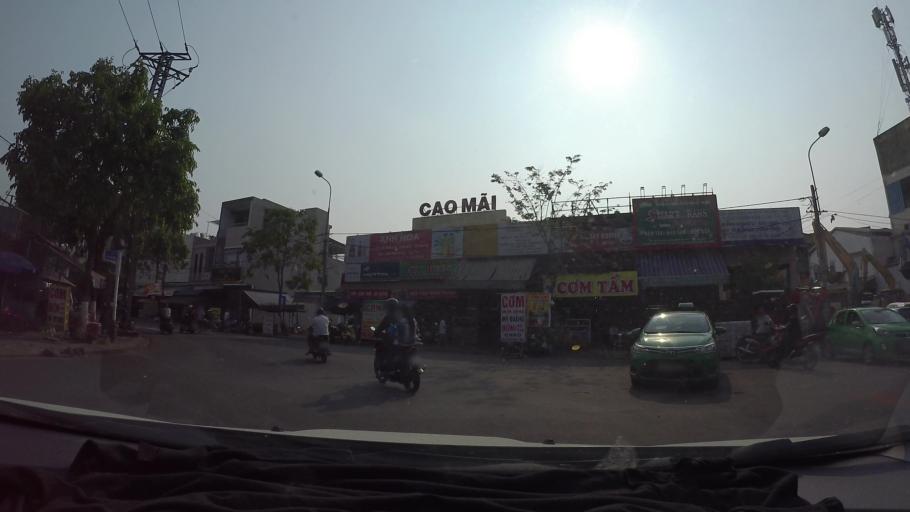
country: VN
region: Da Nang
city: Lien Chieu
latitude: 16.0565
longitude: 108.1721
